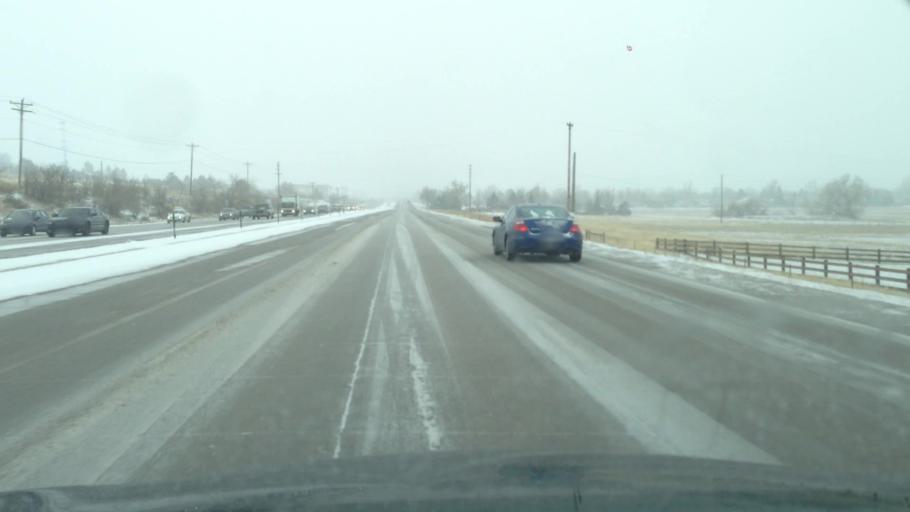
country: US
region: Colorado
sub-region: Douglas County
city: Stonegate
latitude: 39.5686
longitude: -104.7869
